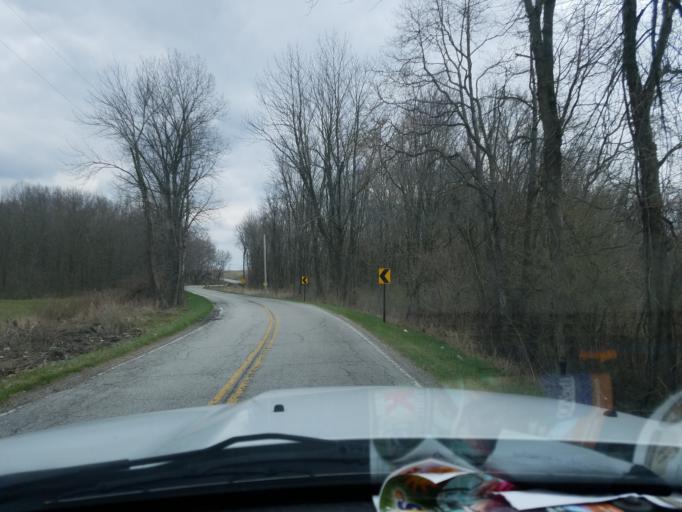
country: US
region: Indiana
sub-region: Vigo County
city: Terre Haute
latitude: 39.4147
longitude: -87.3461
